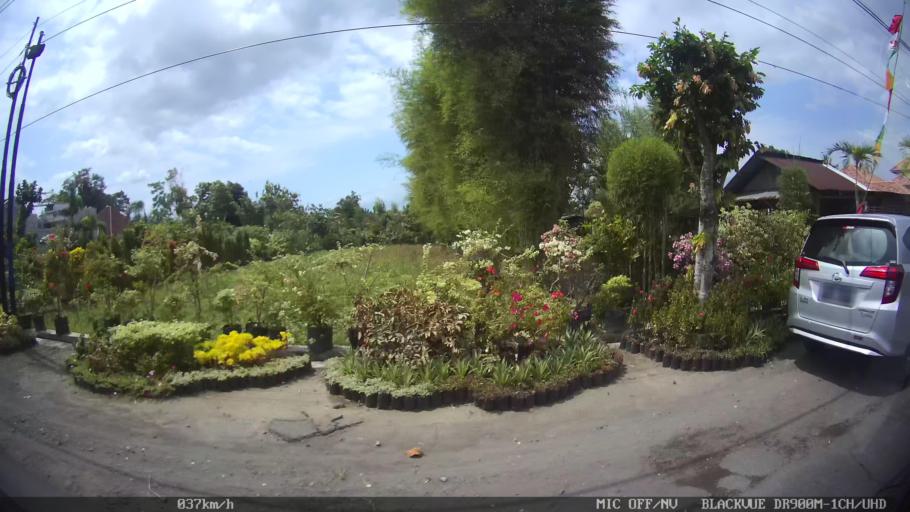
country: ID
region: Daerah Istimewa Yogyakarta
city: Depok
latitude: -7.8002
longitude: 110.4551
